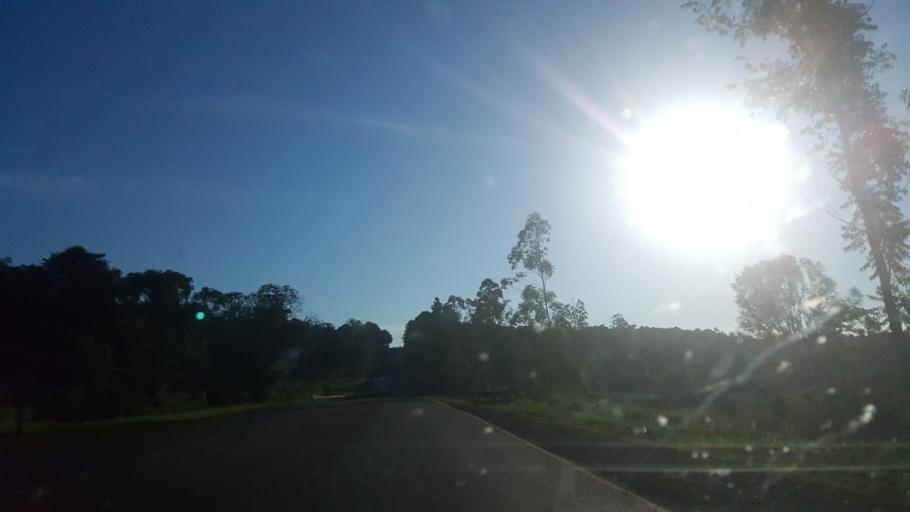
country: AR
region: Misiones
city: Caraguatay
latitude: -26.6652
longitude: -54.7576
